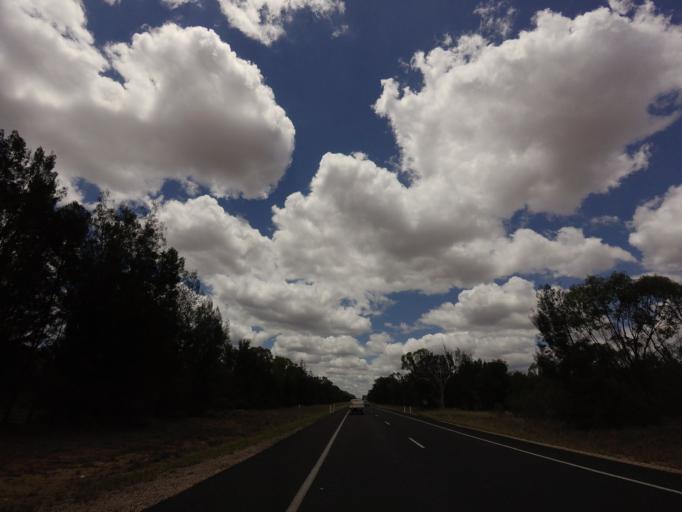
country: AU
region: Queensland
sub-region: Goondiwindi
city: Goondiwindi
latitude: -28.0646
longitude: 150.7598
